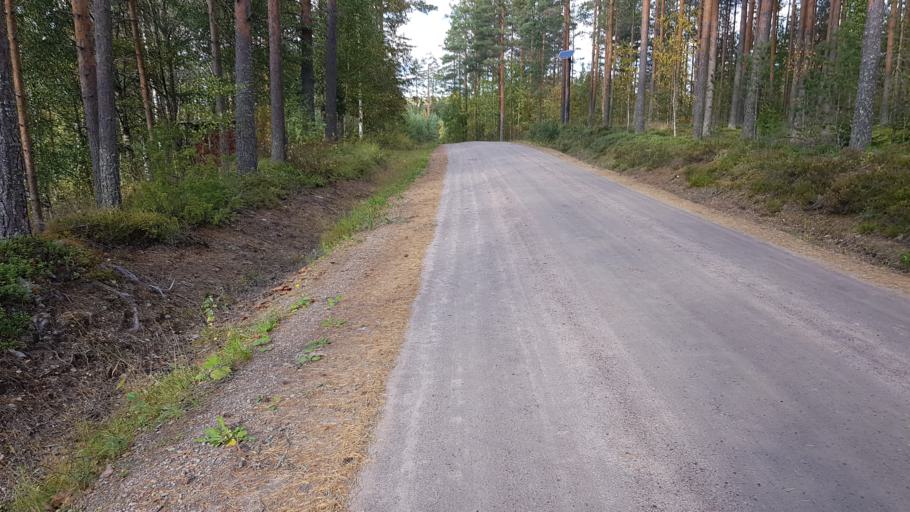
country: FI
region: South Karelia
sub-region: Imatra
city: Ruokolahti
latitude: 61.2533
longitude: 29.0973
